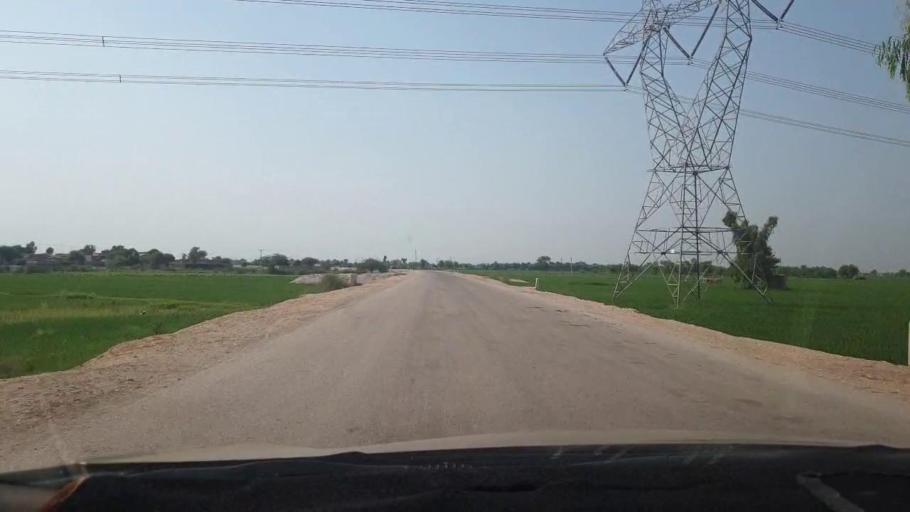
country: PK
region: Sindh
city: Larkana
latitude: 27.6079
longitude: 68.2395
